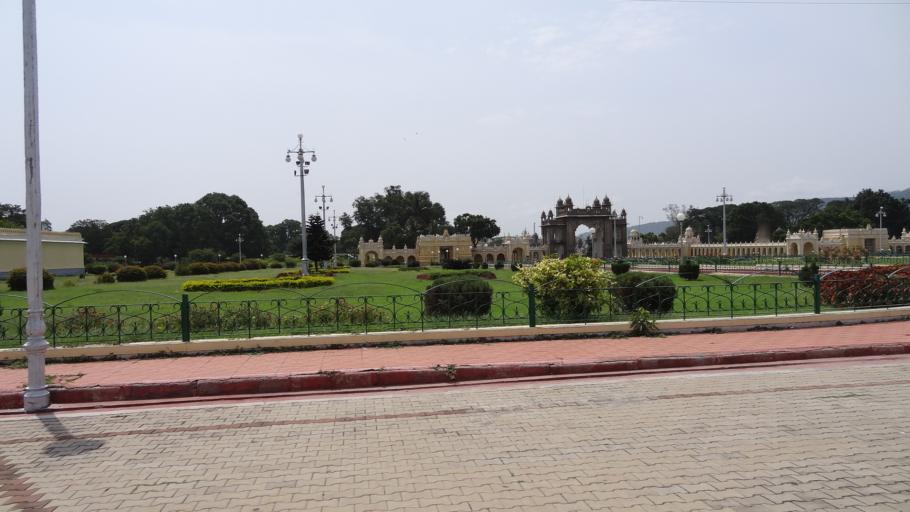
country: IN
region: Karnataka
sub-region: Mysore
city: Mysore
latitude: 12.3061
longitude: 76.6555
